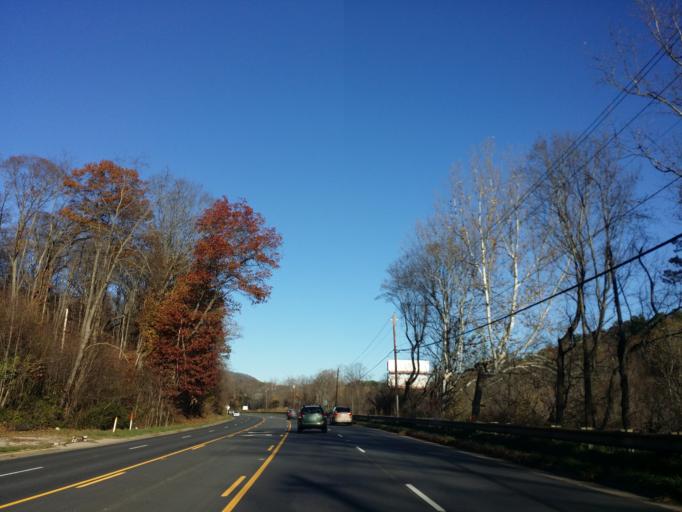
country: US
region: North Carolina
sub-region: Buncombe County
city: Swannanoa
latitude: 35.5849
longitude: -82.4602
